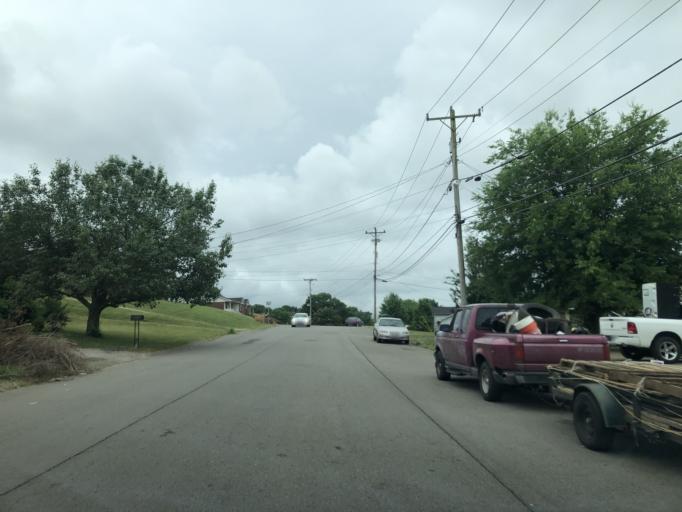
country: US
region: Tennessee
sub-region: Davidson County
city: Goodlettsville
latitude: 36.2589
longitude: -86.7633
